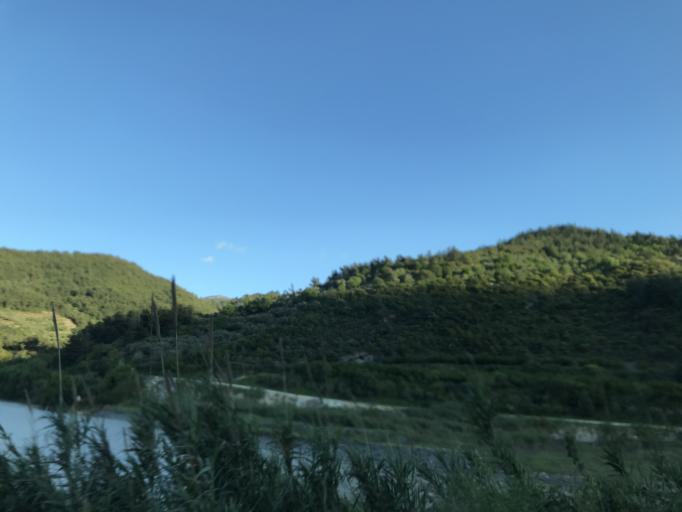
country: TR
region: Hatay
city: Buyukcat
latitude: 36.0905
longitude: 36.0599
